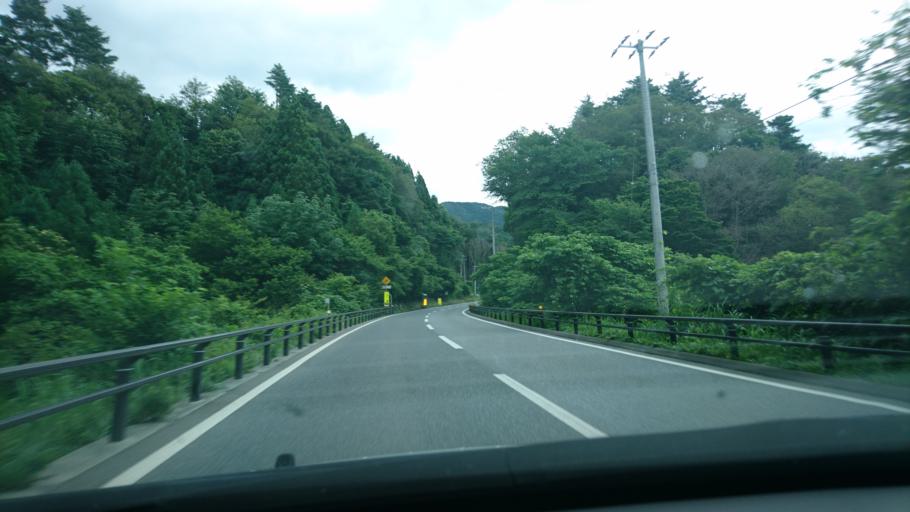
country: JP
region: Iwate
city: Kamaishi
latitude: 39.1569
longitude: 141.8413
